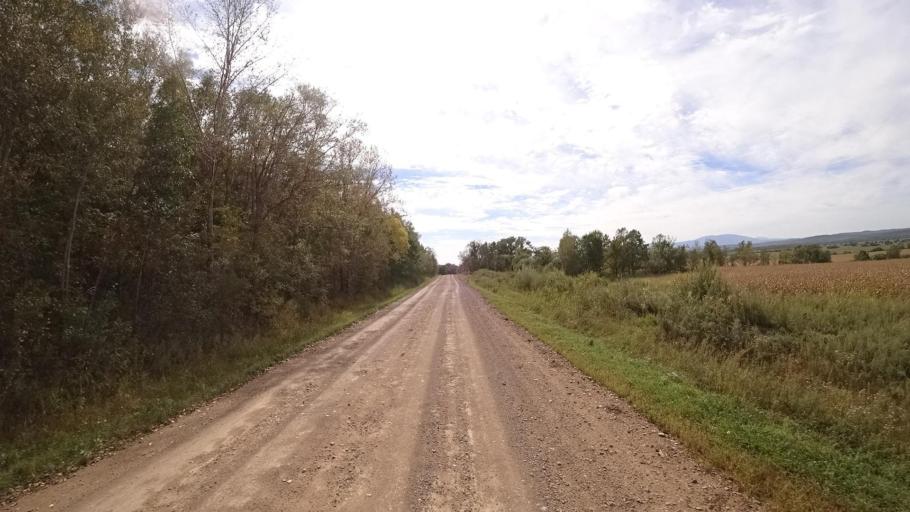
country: RU
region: Primorskiy
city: Yakovlevka
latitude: 44.5756
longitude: 133.5946
